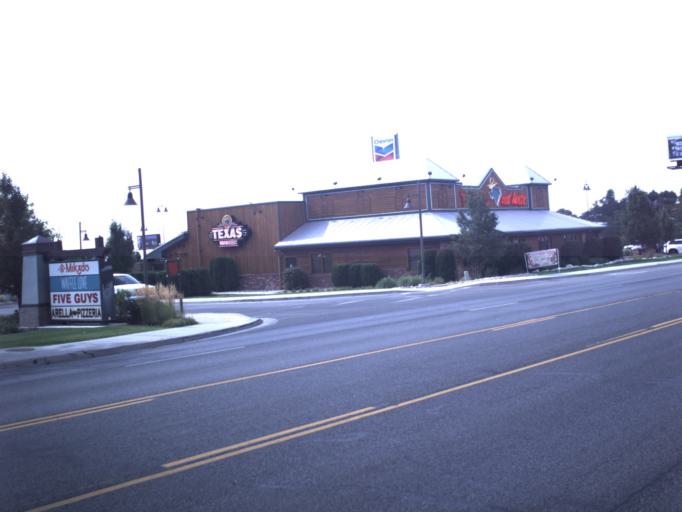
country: US
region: Utah
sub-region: Davis County
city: West Bountiful
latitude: 40.8922
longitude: -111.8921
